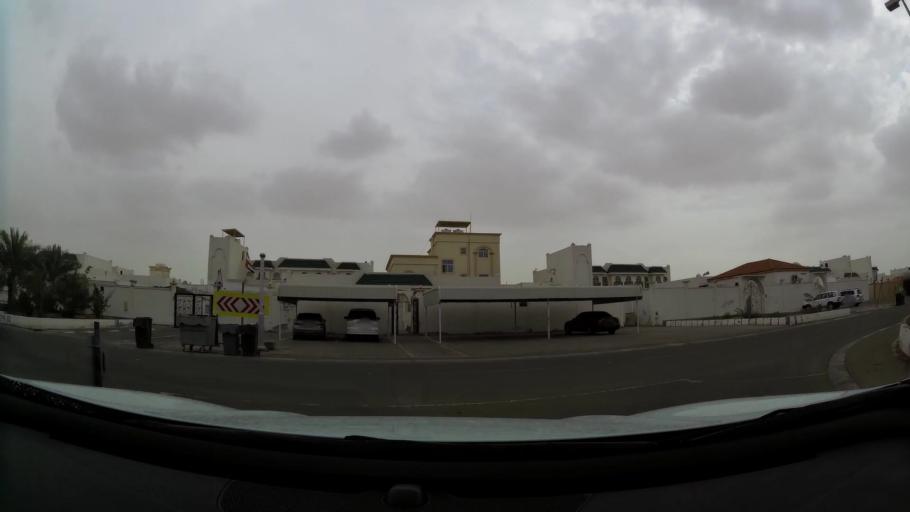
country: AE
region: Abu Dhabi
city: Abu Dhabi
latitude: 24.3554
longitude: 54.6509
